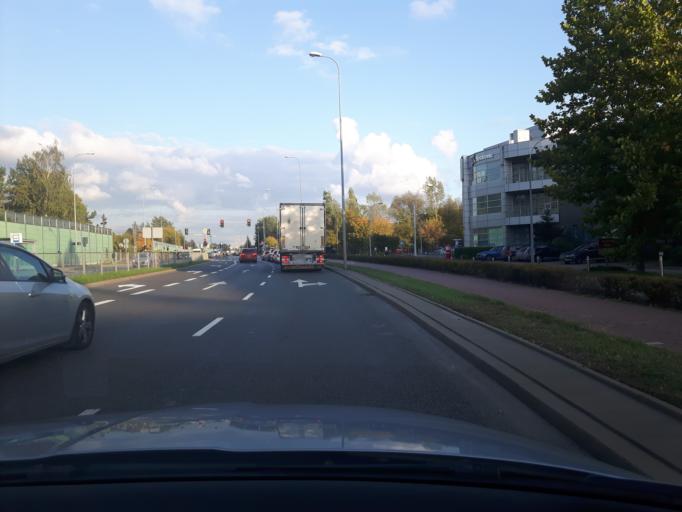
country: PL
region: Masovian Voivodeship
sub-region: Warszawa
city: Ursynow
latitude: 52.1550
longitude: 21.0055
